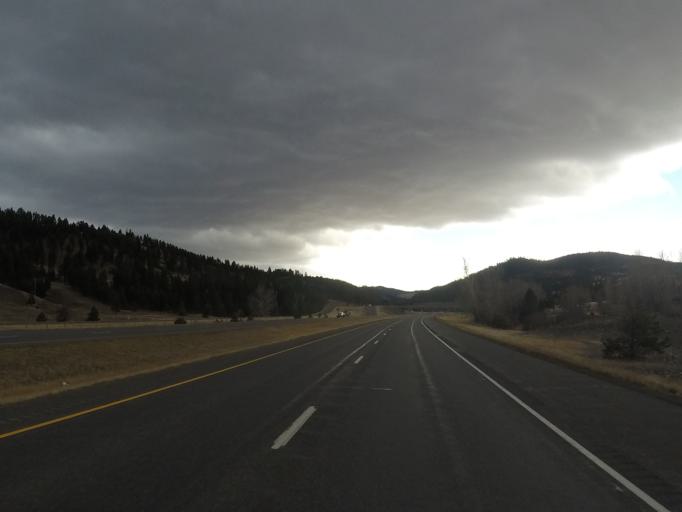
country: US
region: Montana
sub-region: Jefferson County
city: Clancy
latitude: 46.3934
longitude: -112.0213
